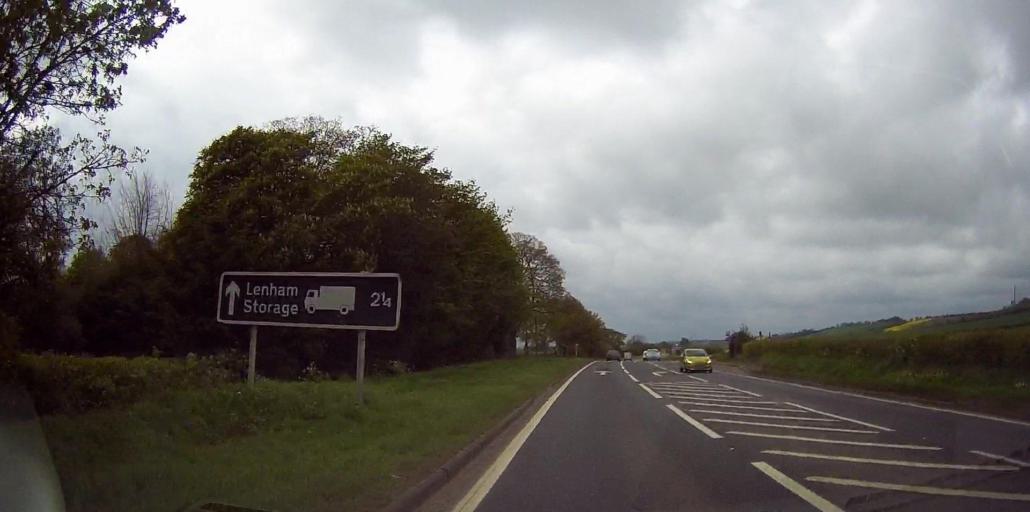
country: GB
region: England
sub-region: Kent
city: Lenham
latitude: 51.2308
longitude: 0.7489
